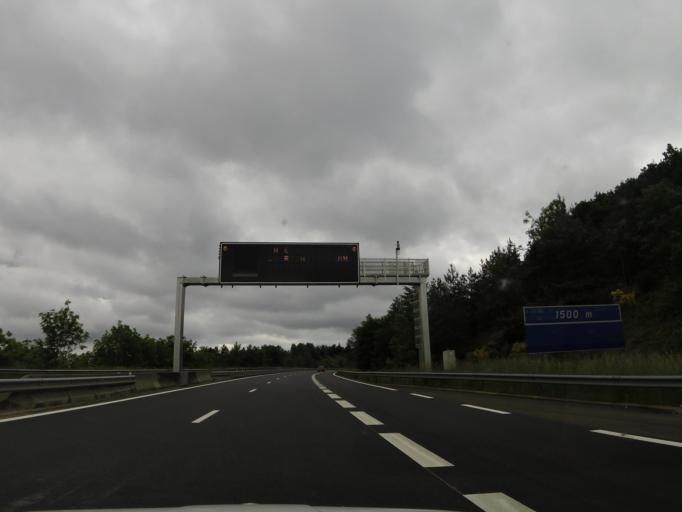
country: FR
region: Rhone-Alpes
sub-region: Departement de la Loire
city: Saint-Just-en-Chevalet
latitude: 45.8632
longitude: 3.8264
